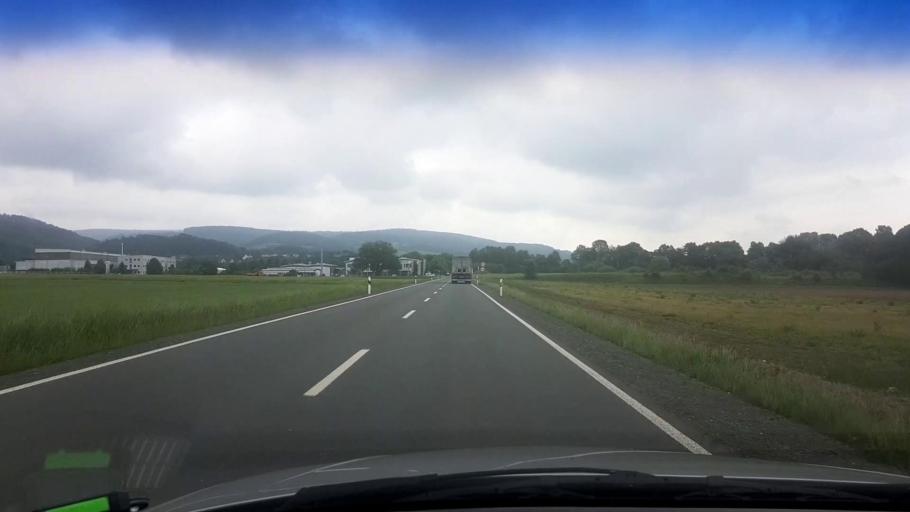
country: DE
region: Bavaria
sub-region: Upper Franconia
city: Gesees
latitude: 50.0154
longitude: 11.6678
